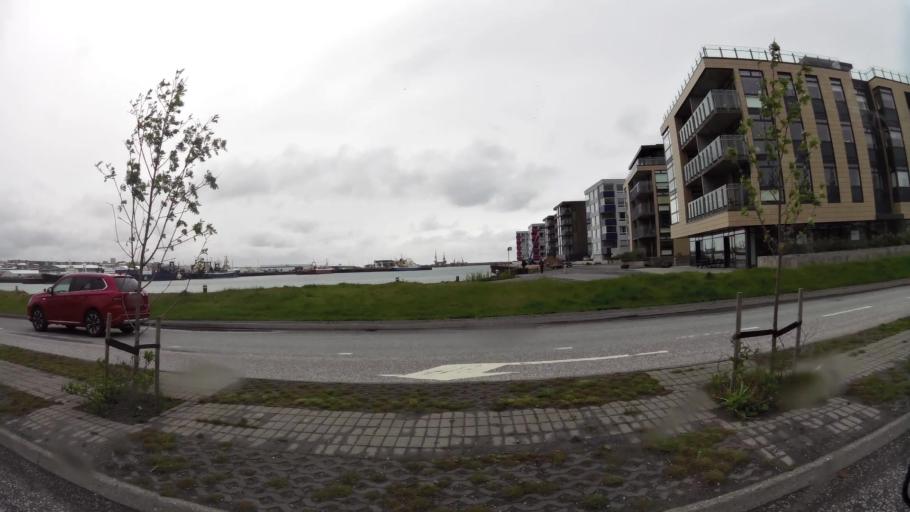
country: IS
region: Capital Region
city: Hafnarfjoerdur
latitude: 64.0692
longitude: -21.9593
